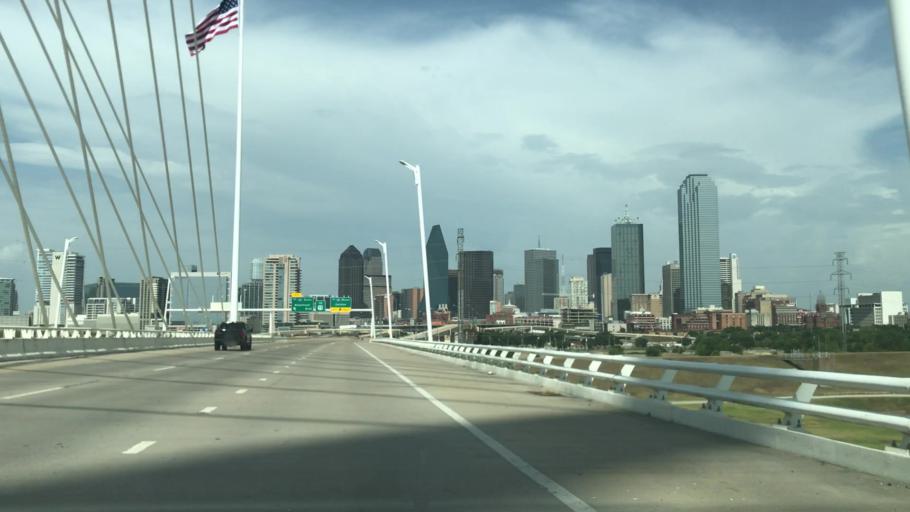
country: US
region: Texas
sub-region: Dallas County
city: Dallas
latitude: 32.7802
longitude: -96.8213
